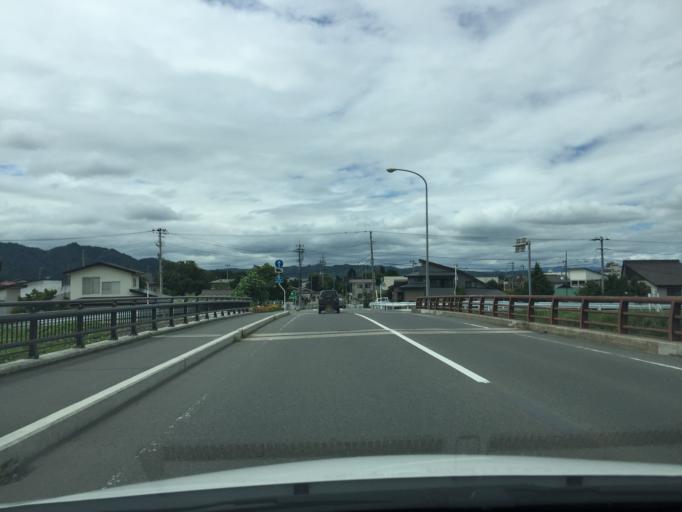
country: JP
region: Yamagata
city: Yonezawa
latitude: 37.9007
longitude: 140.1218
